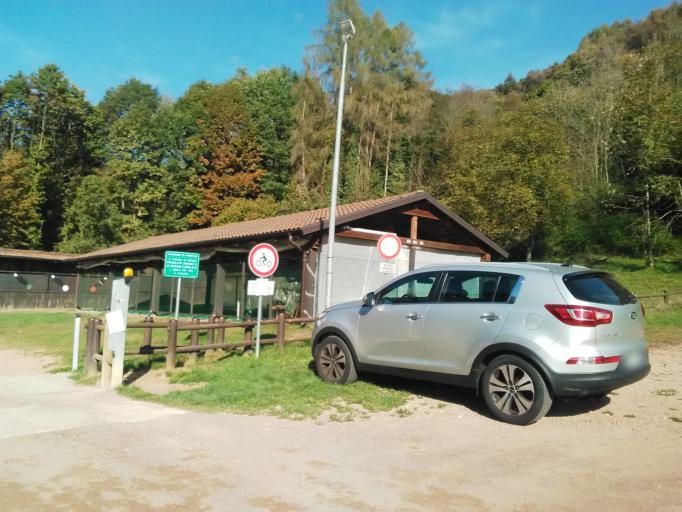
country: IT
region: Piedmont
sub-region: Provincia di Vercelli
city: Postua
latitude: 45.7232
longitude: 8.2179
